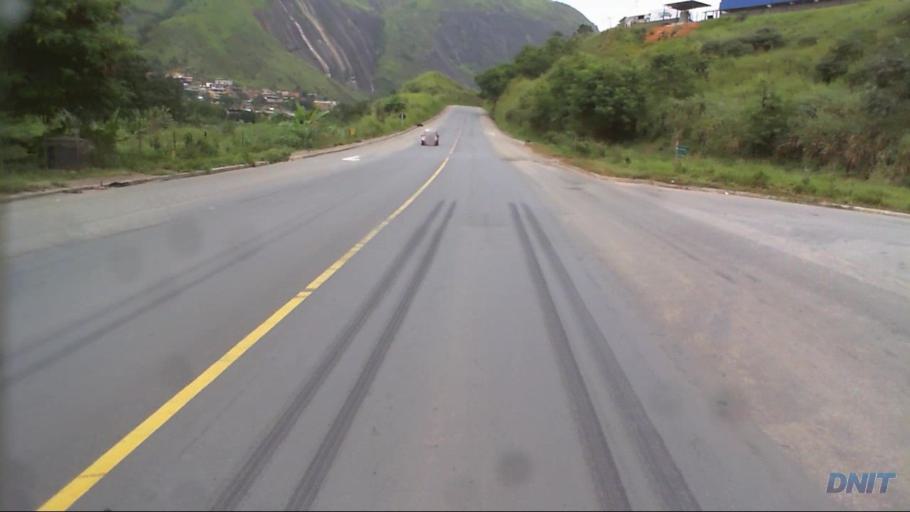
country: BR
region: Minas Gerais
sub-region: Coronel Fabriciano
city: Coronel Fabriciano
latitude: -19.5312
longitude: -42.6723
